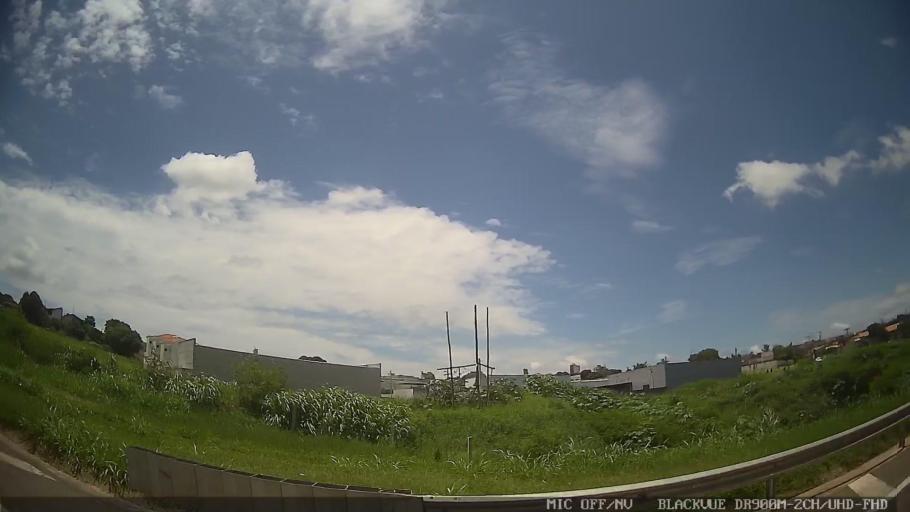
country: BR
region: Sao Paulo
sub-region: Laranjal Paulista
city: Laranjal Paulista
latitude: -23.0409
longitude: -47.8401
